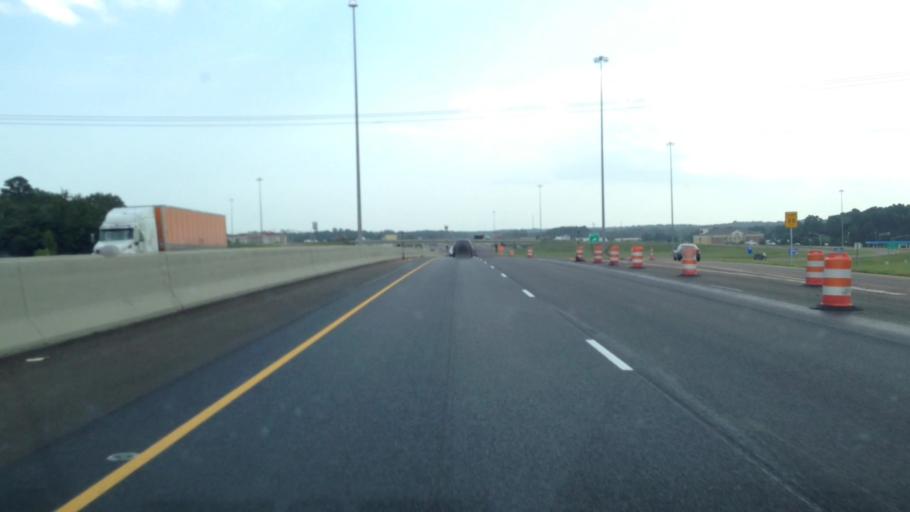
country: US
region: Mississippi
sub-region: Hinds County
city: Byram
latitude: 32.1799
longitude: -90.2595
